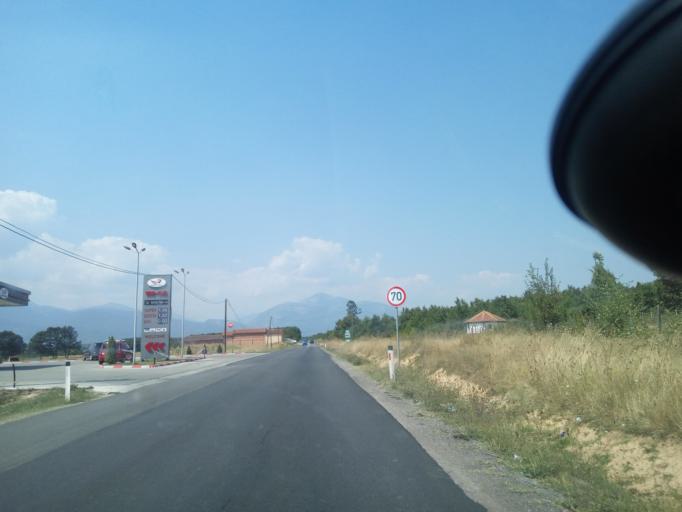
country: XK
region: Gjakova
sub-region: Komuna e Decanit
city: Gllogjan
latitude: 42.4510
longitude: 20.3604
